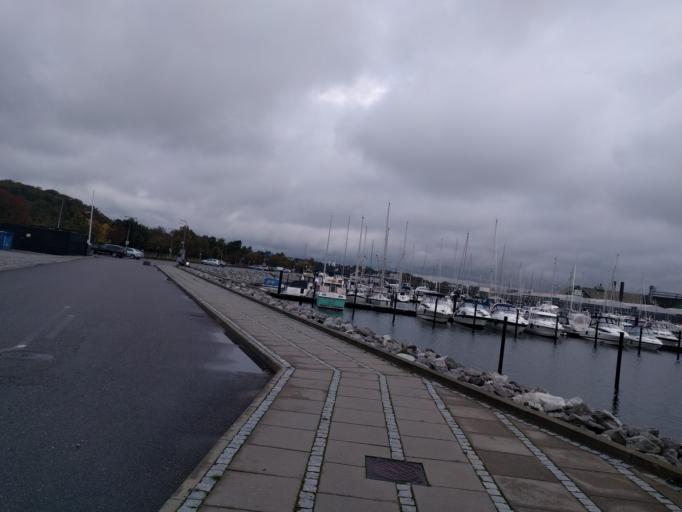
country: DK
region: South Denmark
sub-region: Fredericia Kommune
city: Fredericia
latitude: 55.5526
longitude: 9.7270
